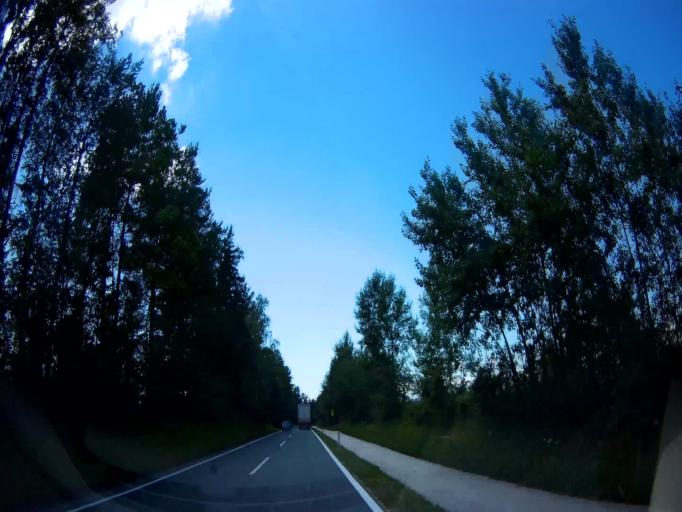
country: AT
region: Carinthia
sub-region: Politischer Bezirk Volkermarkt
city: Eberndorf
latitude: 46.6080
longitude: 14.6914
